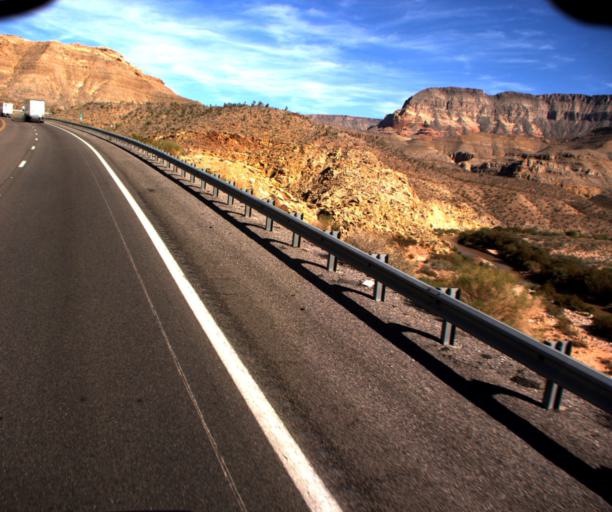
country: US
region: Arizona
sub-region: Mohave County
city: Beaver Dam
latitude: 36.9576
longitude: -113.7874
